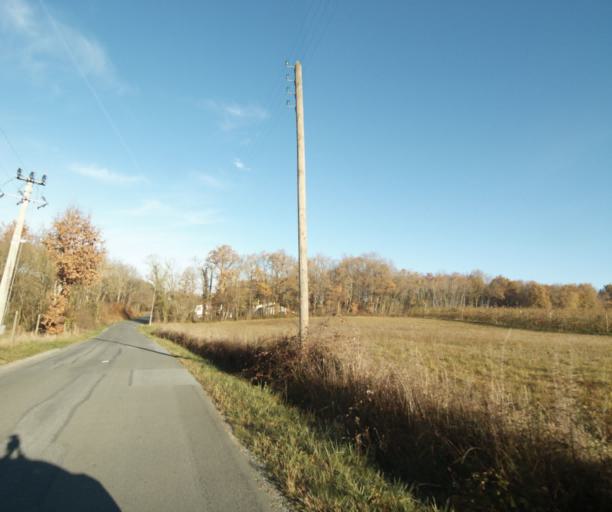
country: FR
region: Poitou-Charentes
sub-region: Departement de la Charente-Maritime
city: Fontcouverte
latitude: 45.7504
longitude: -0.5645
